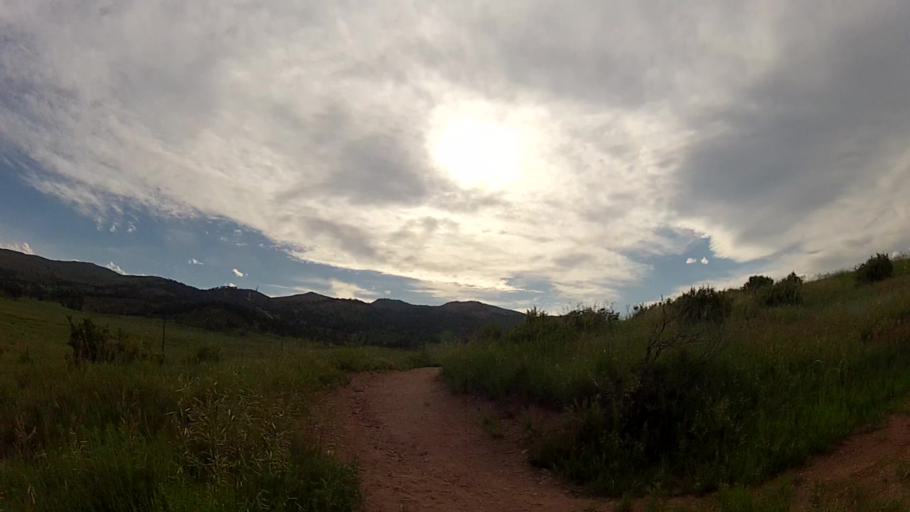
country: US
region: Colorado
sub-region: Larimer County
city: Laporte
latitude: 40.4900
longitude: -105.2332
